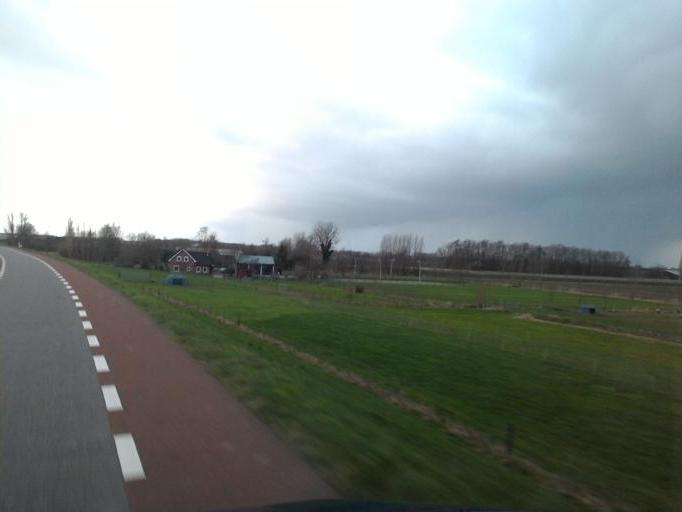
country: NL
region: Gelderland
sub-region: Gemeente Culemborg
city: Culemborg
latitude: 51.9721
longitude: 5.2229
